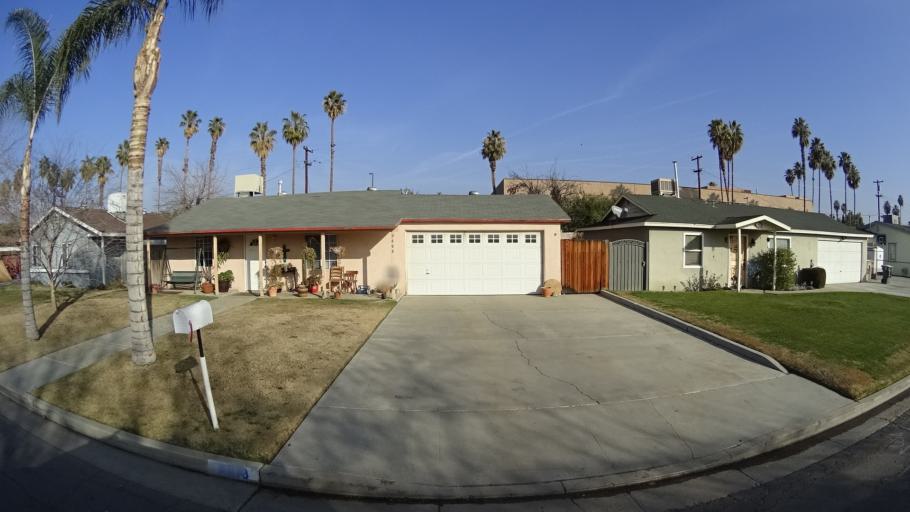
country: US
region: California
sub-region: Kern County
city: Bakersfield
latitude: 35.3355
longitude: -119.0319
